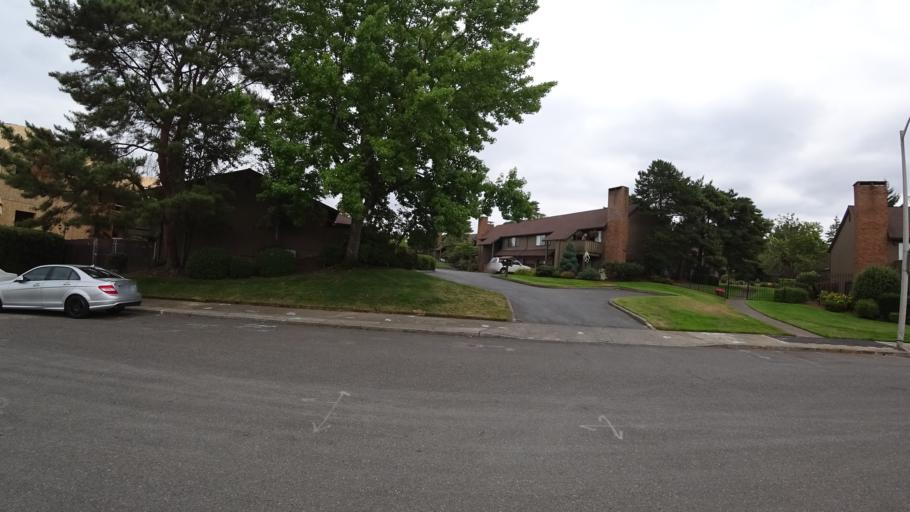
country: US
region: Oregon
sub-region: Multnomah County
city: Fairview
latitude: 45.5446
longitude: -122.5123
